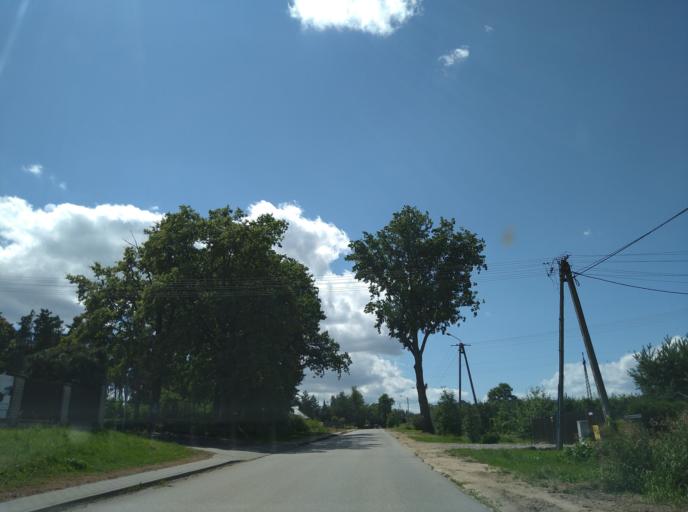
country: PL
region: Masovian Voivodeship
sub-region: Powiat bialobrzeski
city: Promna
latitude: 51.6734
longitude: 20.9387
